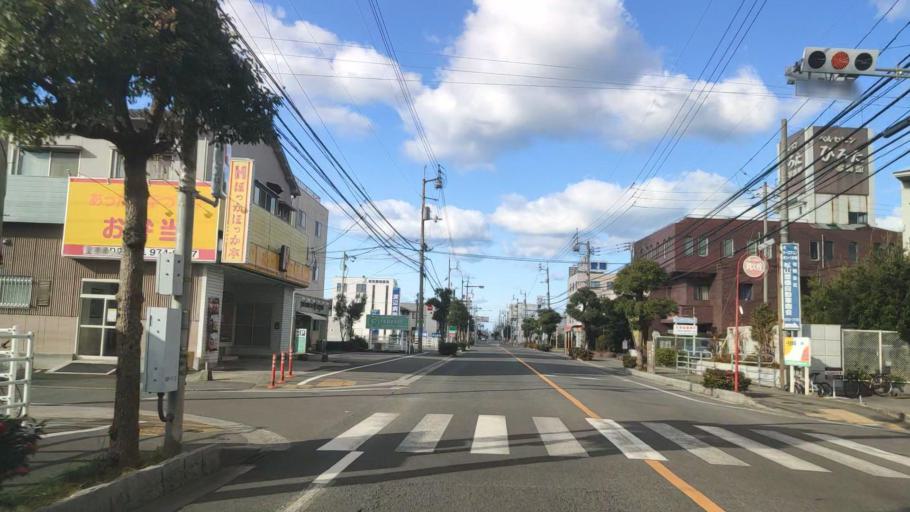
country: JP
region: Ehime
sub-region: Shikoku-chuo Shi
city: Matsuyama
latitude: 33.8284
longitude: 132.7279
